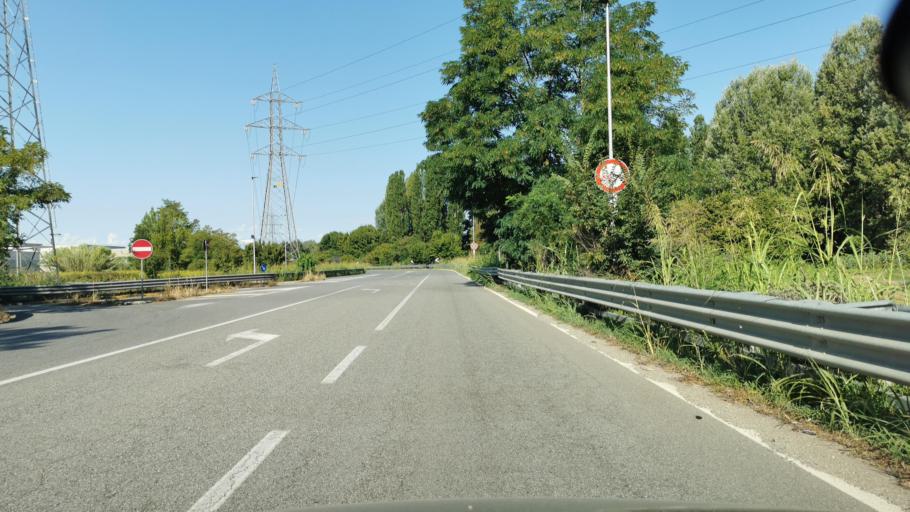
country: IT
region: Piedmont
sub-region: Provincia di Torino
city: Settimo Torinese
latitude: 45.1606
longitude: 7.7684
